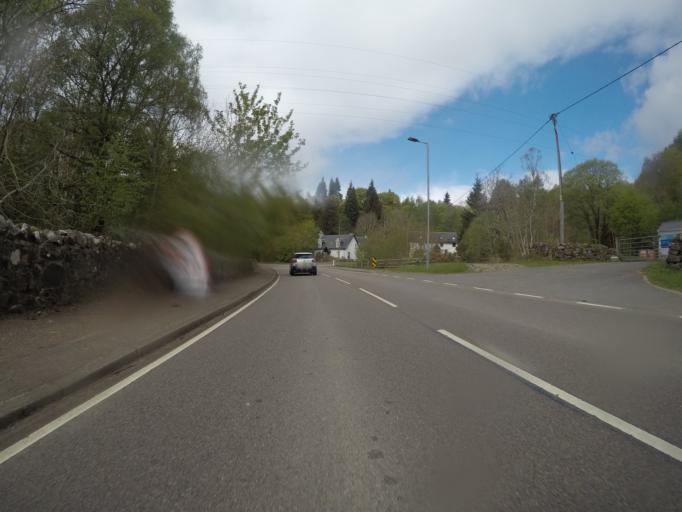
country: GB
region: Scotland
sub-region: Highland
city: Spean Bridge
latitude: 57.0699
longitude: -4.8098
